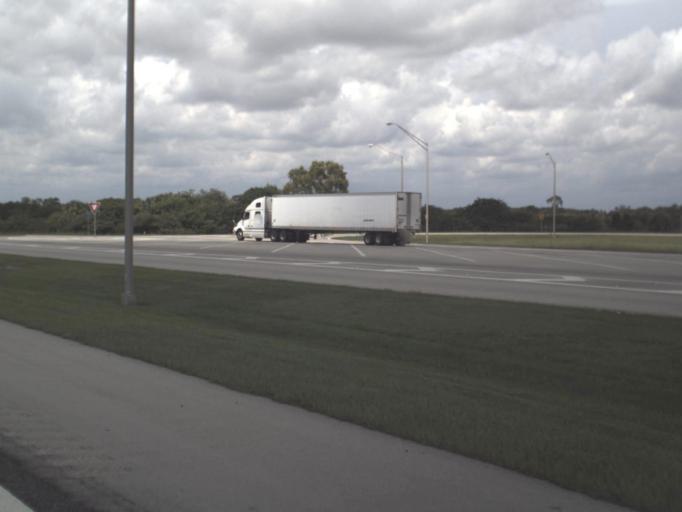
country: US
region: Florida
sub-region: Charlotte County
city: Charlotte Park
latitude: 26.8797
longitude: -81.9854
